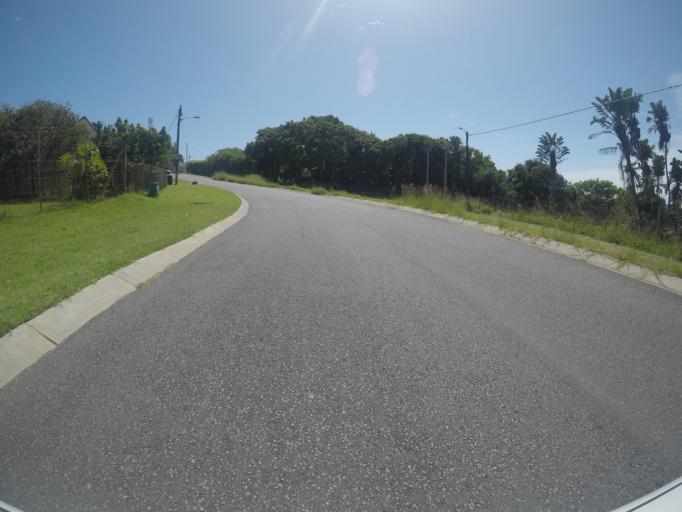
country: ZA
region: Eastern Cape
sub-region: Buffalo City Metropolitan Municipality
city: East London
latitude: -32.9425
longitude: 28.0238
